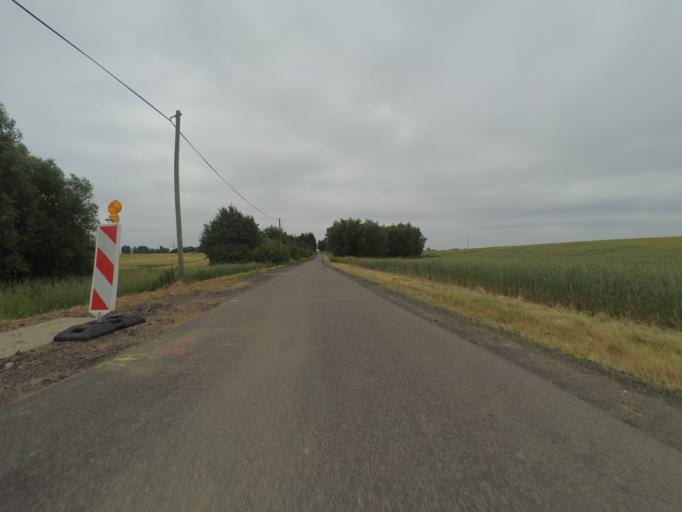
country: DE
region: Mecklenburg-Vorpommern
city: Sternberg
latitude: 53.6965
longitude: 11.8601
